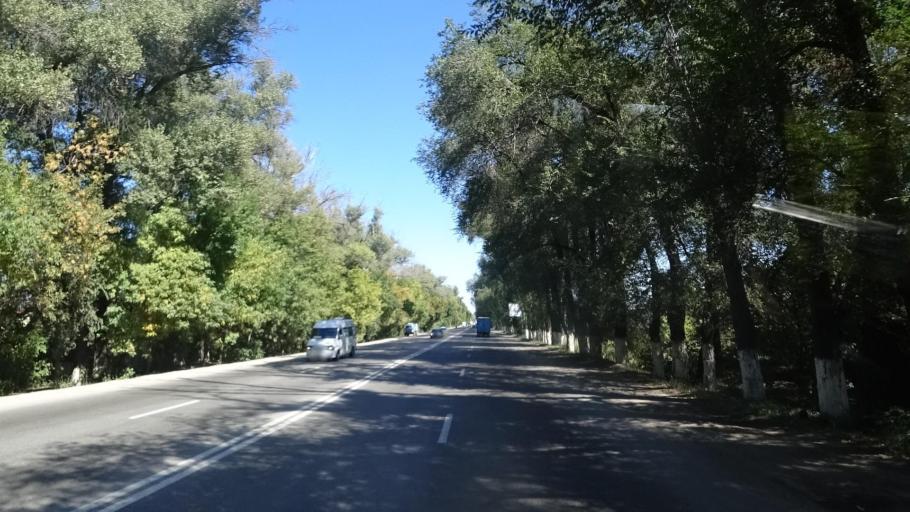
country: KZ
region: Almaty Oblysy
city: Pervomayskiy
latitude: 43.3229
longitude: 77.0283
